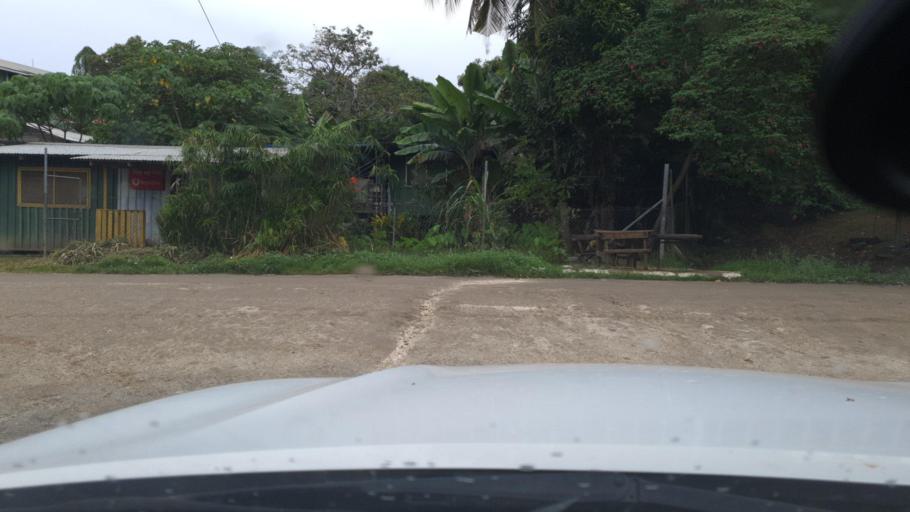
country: SB
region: Guadalcanal
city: Honiara
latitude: -9.4504
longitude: 159.9825
